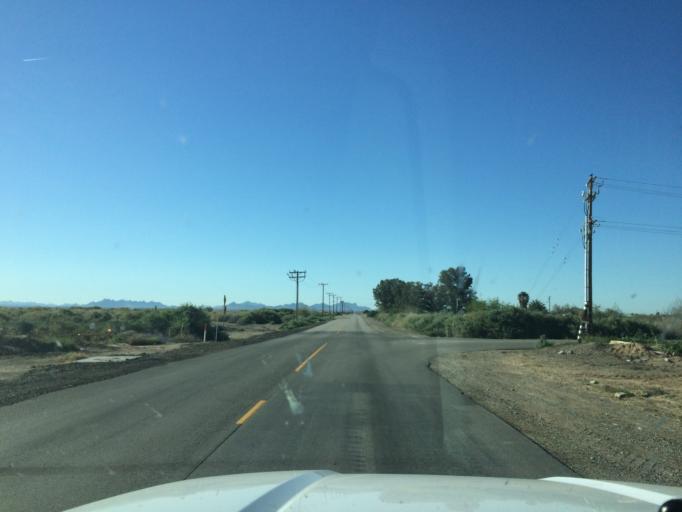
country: US
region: California
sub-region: Riverside County
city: Blythe
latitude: 33.6040
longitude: -114.5707
